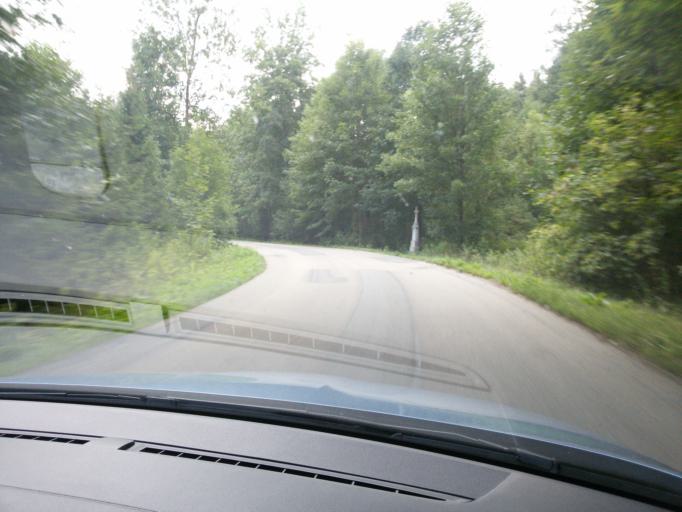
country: CZ
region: South Moravian
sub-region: Okres Brno-Venkov
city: Lomnice
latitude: 49.4207
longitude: 16.4260
